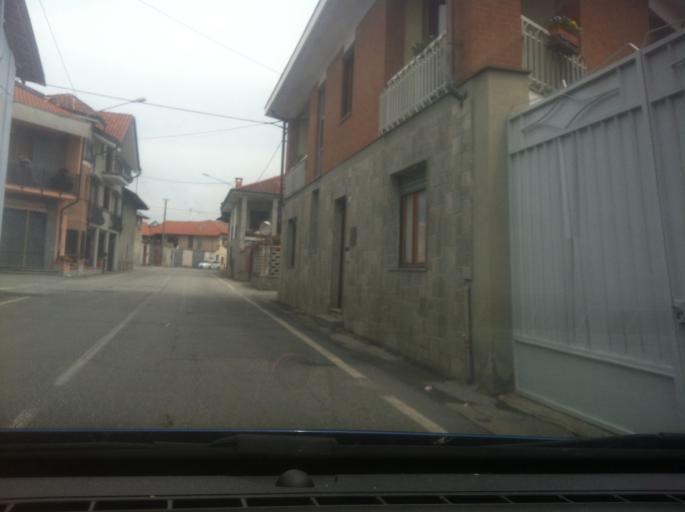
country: IT
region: Piedmont
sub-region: Provincia di Torino
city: Foglizzo
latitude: 45.2678
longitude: 7.8171
